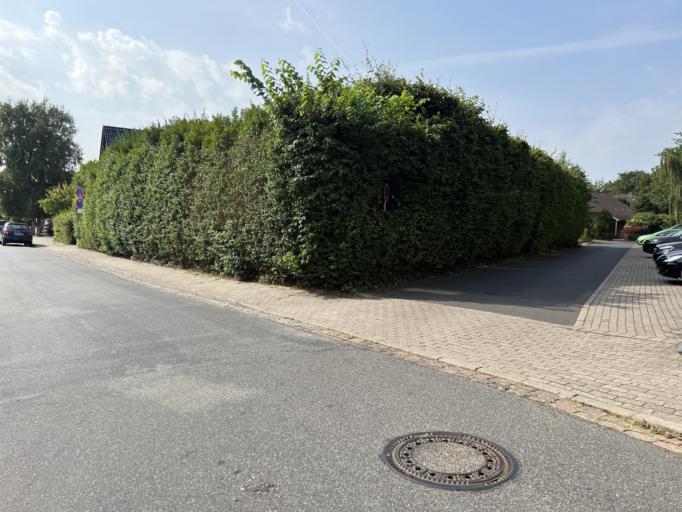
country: DE
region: Schleswig-Holstein
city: Wesseln
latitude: 54.1989
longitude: 9.0803
